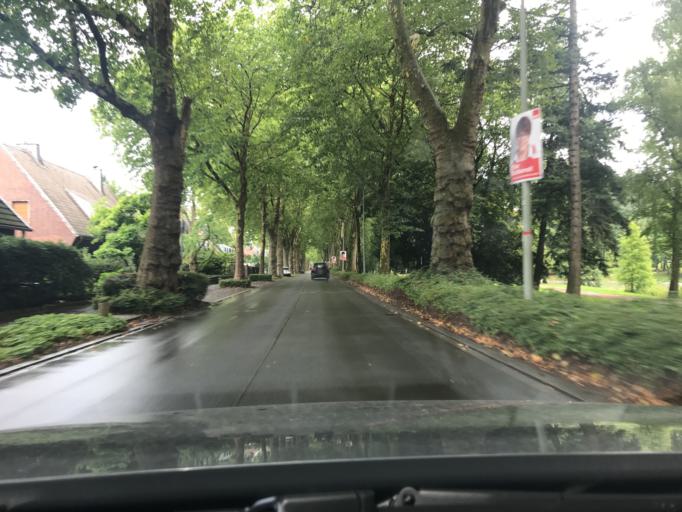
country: DE
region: North Rhine-Westphalia
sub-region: Regierungsbezirk Dusseldorf
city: Krefeld
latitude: 51.3444
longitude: 6.5893
